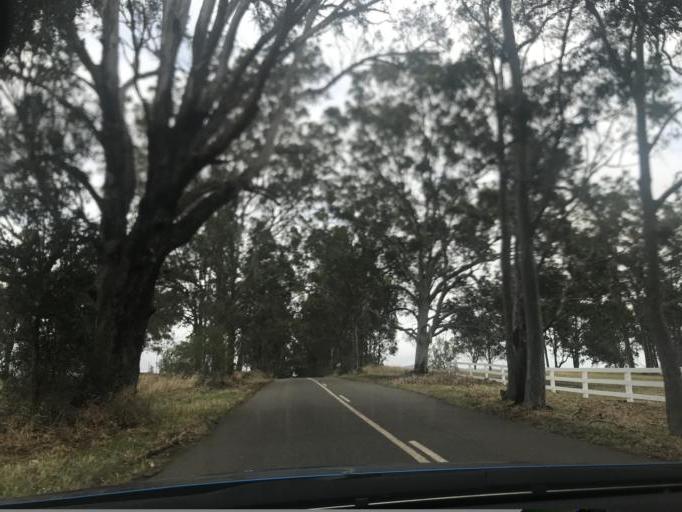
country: AU
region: New South Wales
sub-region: Cessnock
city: Cessnock
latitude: -32.8111
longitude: 151.3062
